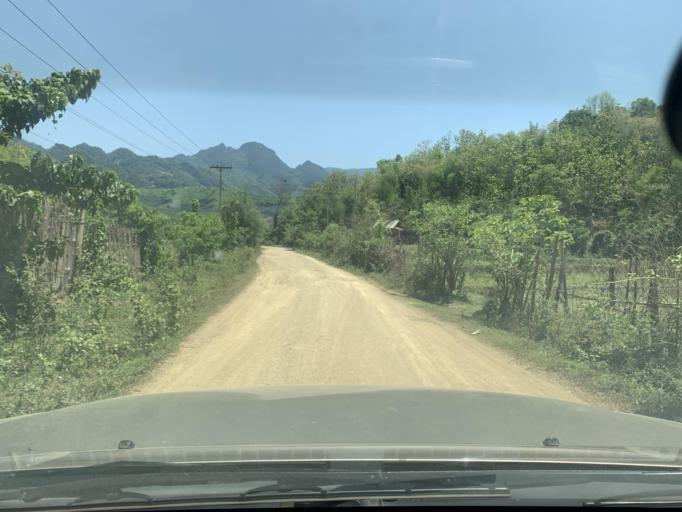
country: LA
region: Louangphabang
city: Louangphabang
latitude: 19.9053
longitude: 102.2482
